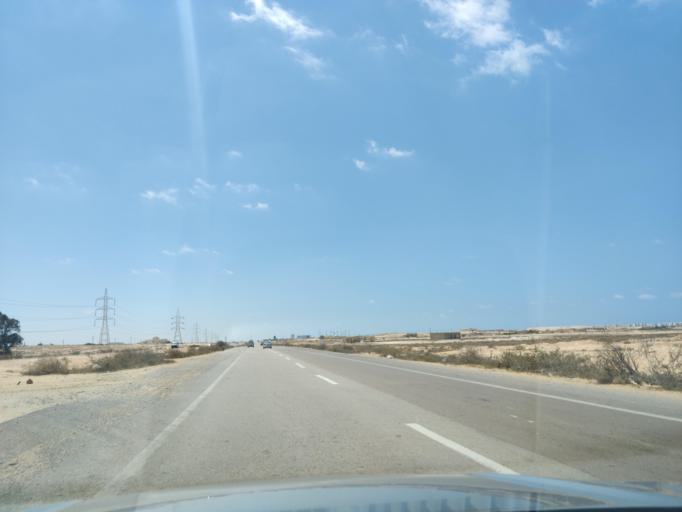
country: EG
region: Muhafazat Matruh
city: Al `Alamayn
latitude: 31.0667
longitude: 28.1793
